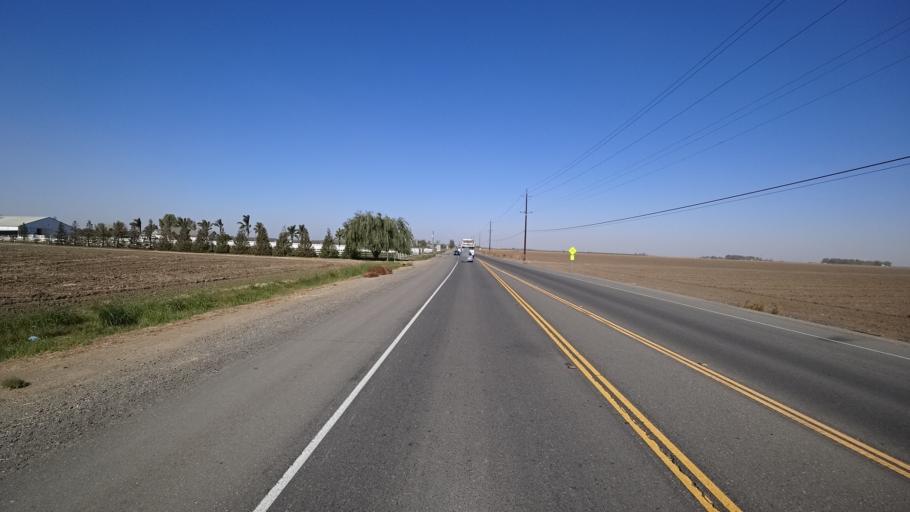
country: US
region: California
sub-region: Yolo County
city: Davis
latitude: 38.5928
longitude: -121.7303
